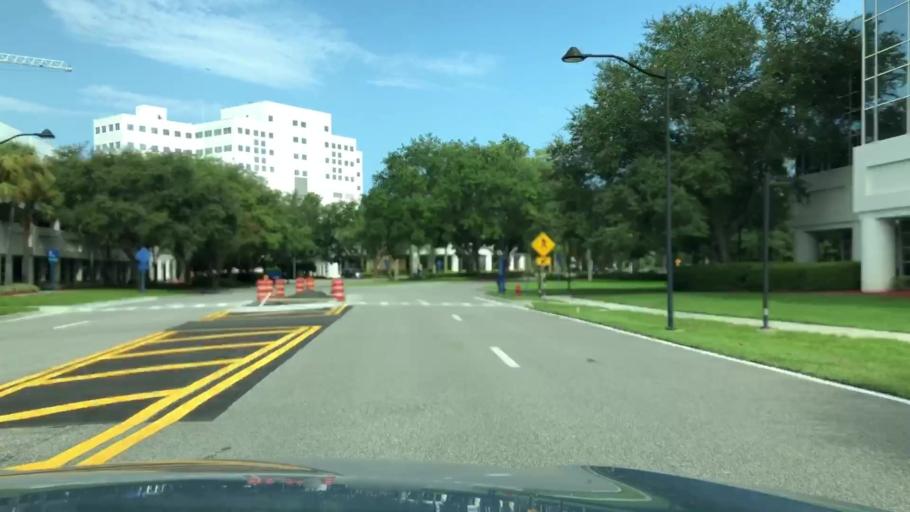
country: US
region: Florida
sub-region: Duval County
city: Jacksonville Beach
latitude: 30.2627
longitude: -81.4435
